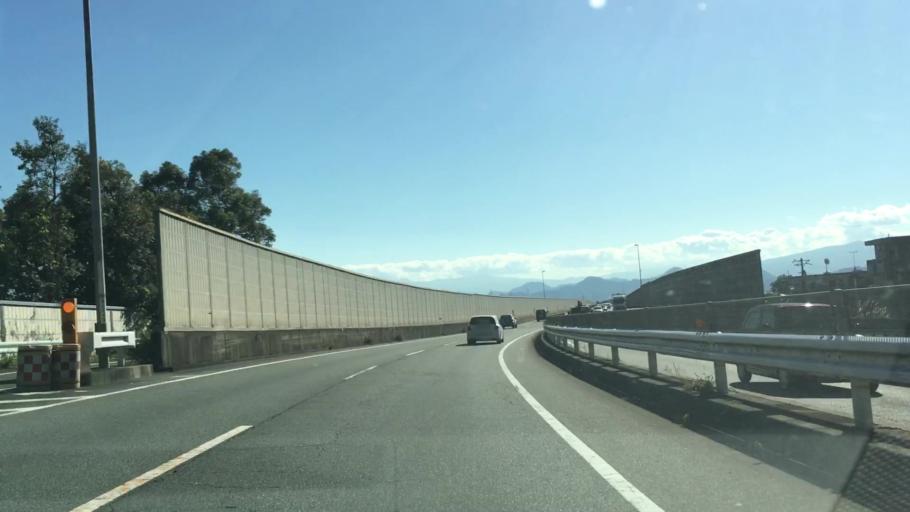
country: JP
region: Shizuoka
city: Mishima
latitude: 35.1715
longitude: 138.9014
